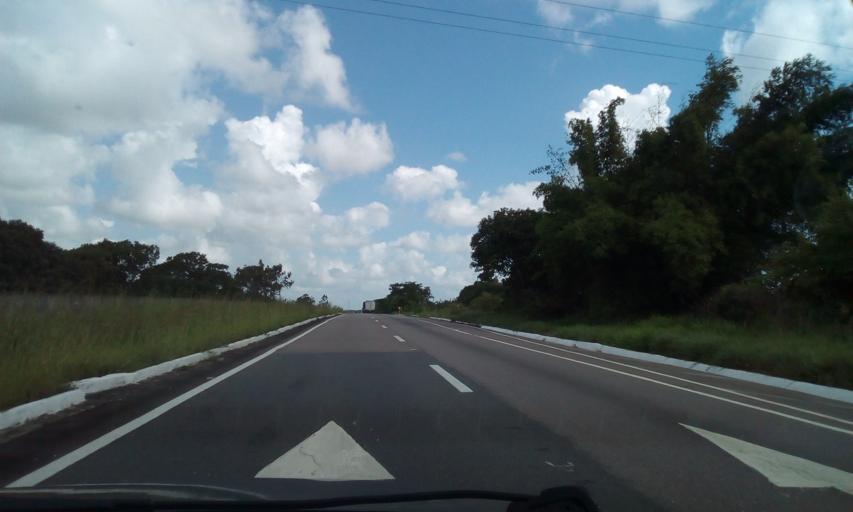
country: BR
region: Paraiba
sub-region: Conde
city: Conde
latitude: -7.2999
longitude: -34.9386
